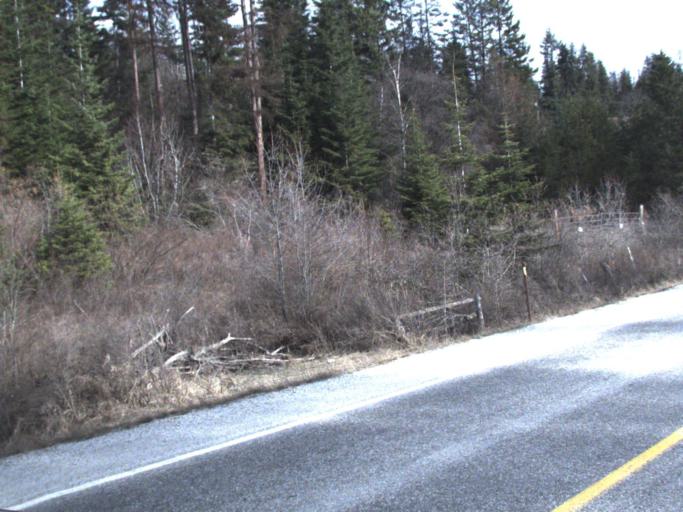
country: US
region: Washington
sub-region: Pend Oreille County
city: Newport
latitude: 48.4817
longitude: -117.2735
